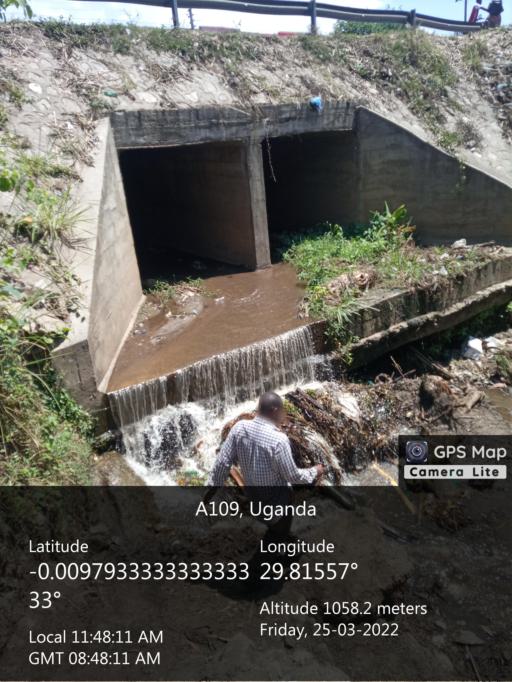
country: UG
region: Western Region
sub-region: Kasese District
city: Kilembe
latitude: -0.0098
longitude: 29.8156
